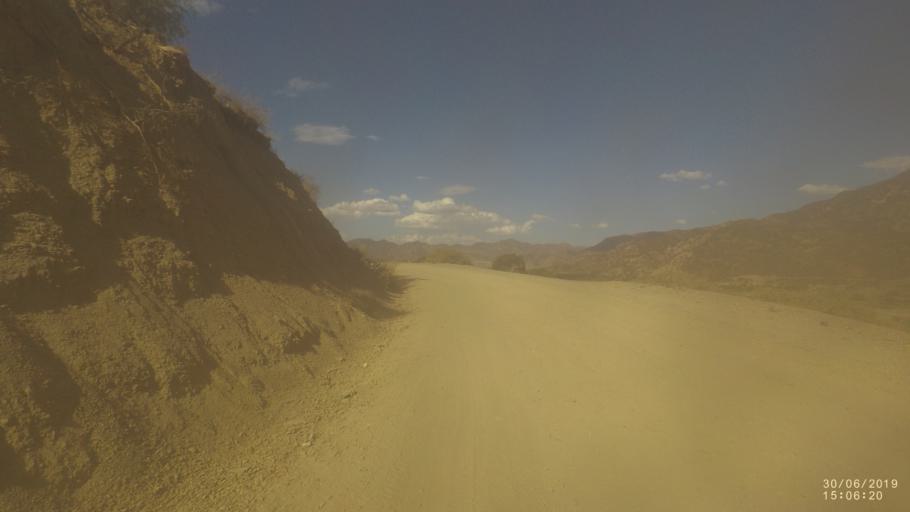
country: BO
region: Cochabamba
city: Irpa Irpa
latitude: -17.7320
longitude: -66.3118
